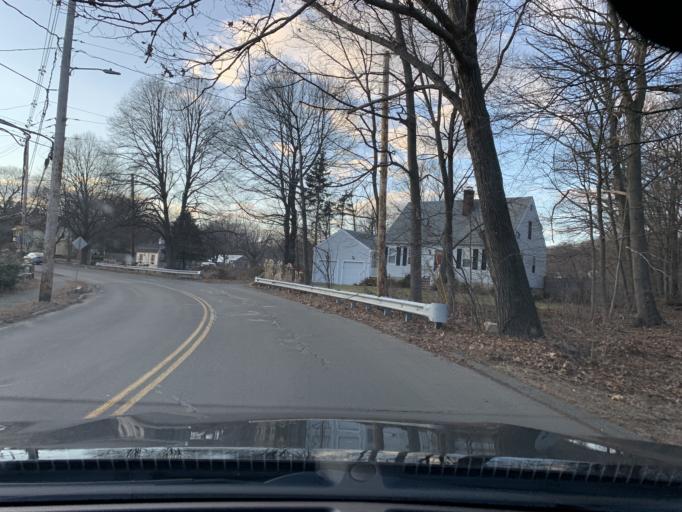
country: US
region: Massachusetts
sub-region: Essex County
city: Danvers
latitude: 42.5664
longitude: -70.9549
